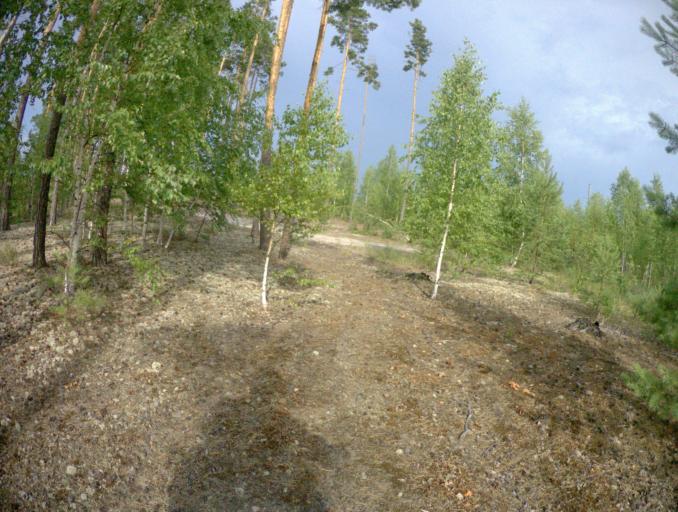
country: RU
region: Ivanovo
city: Talitsy
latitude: 56.4408
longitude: 42.3130
